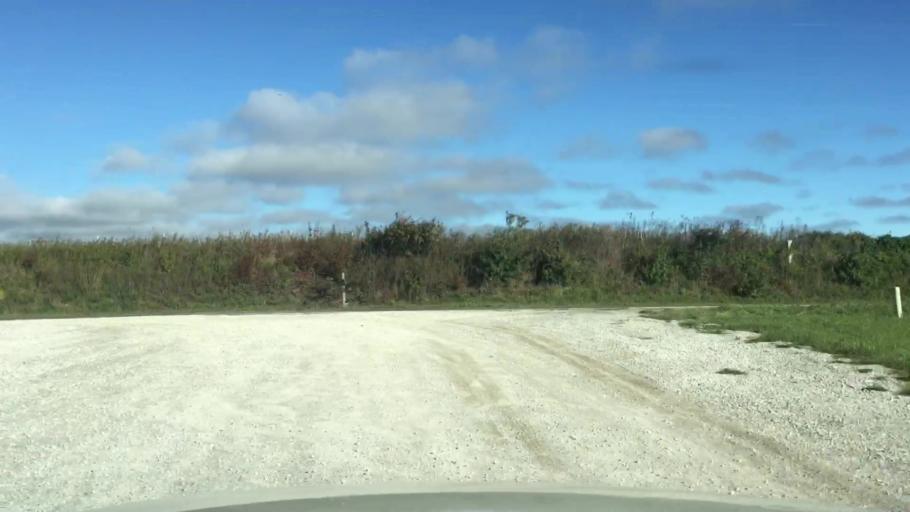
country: US
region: Missouri
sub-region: Howard County
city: Fayette
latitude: 39.1118
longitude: -92.7265
